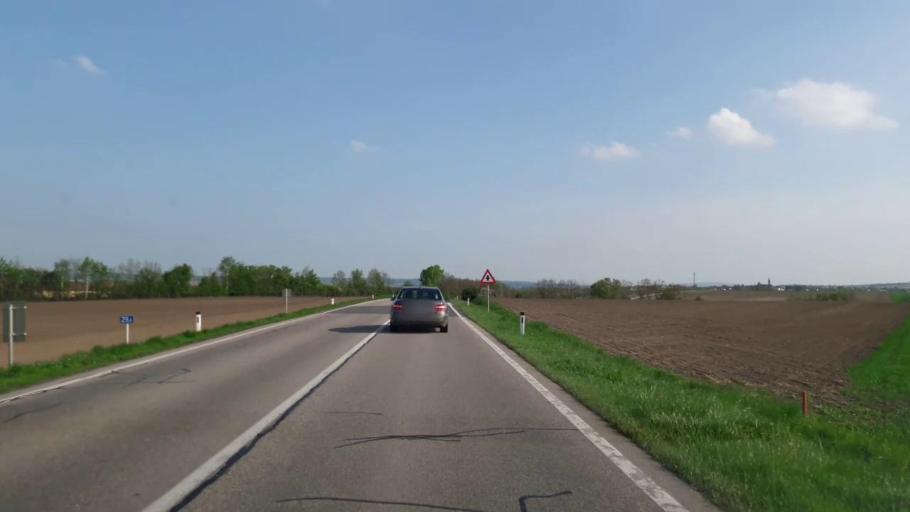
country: AT
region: Lower Austria
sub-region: Politischer Bezirk Hollabrunn
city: Guntersdorf
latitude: 48.6205
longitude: 16.0664
